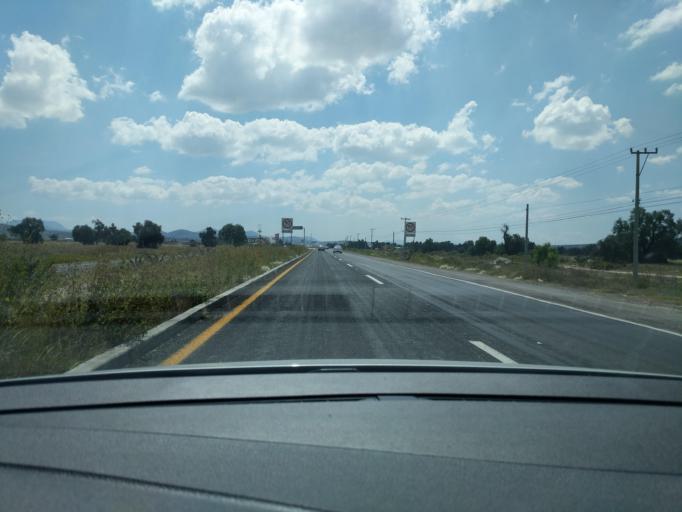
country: MX
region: Hidalgo
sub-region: Mineral de la Reforma
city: Rinconada de los Angeles
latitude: 19.9785
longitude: -98.7016
